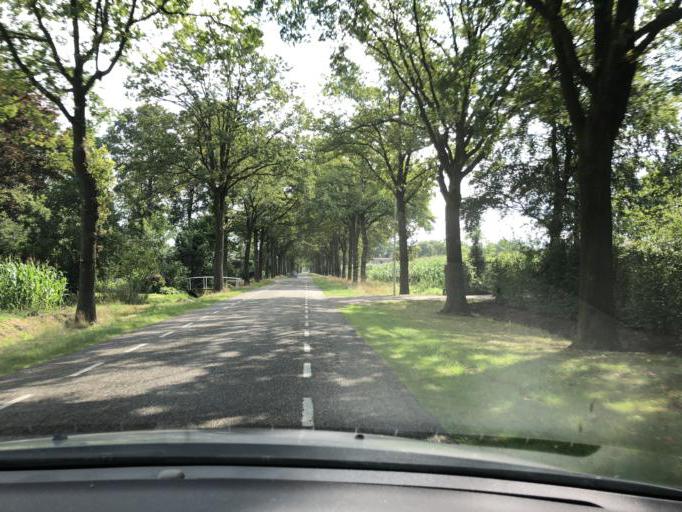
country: NL
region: Overijssel
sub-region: Gemeente Dalfsen
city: Dalfsen
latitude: 52.5772
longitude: 6.3218
